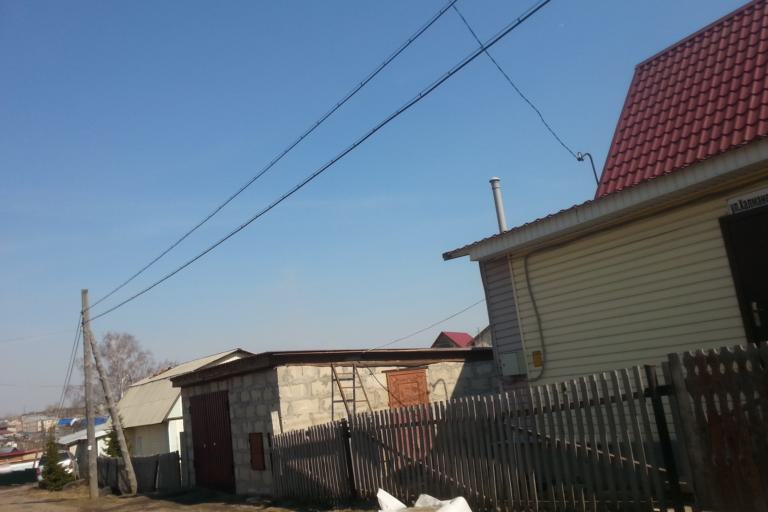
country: RU
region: Altai Krai
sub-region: Gorod Barnaulskiy
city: Barnaul
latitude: 53.3754
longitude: 83.6937
